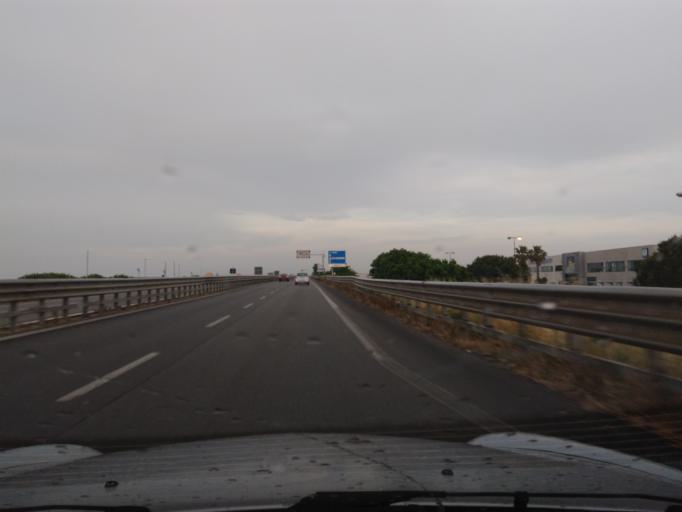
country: IT
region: Apulia
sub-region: Provincia di Bari
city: Molfetta
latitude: 41.2066
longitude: 16.5620
